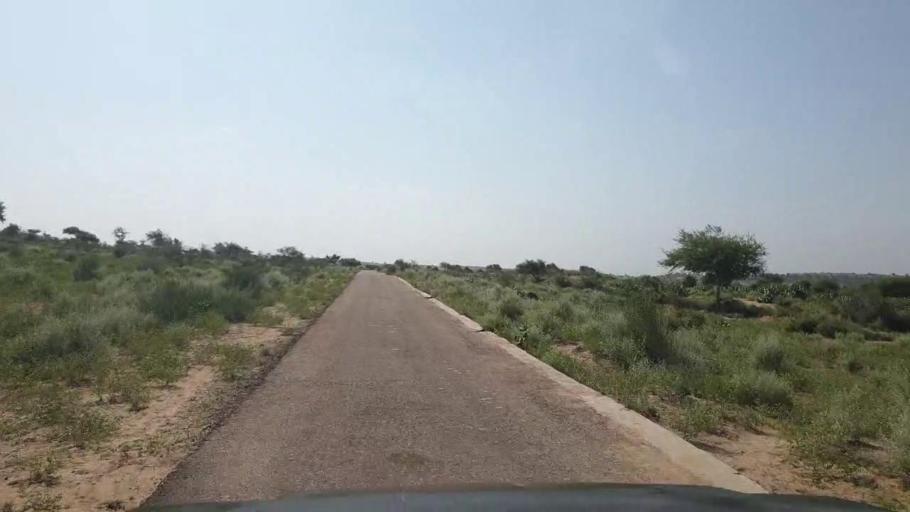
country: PK
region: Sindh
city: Islamkot
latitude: 25.1756
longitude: 70.3966
